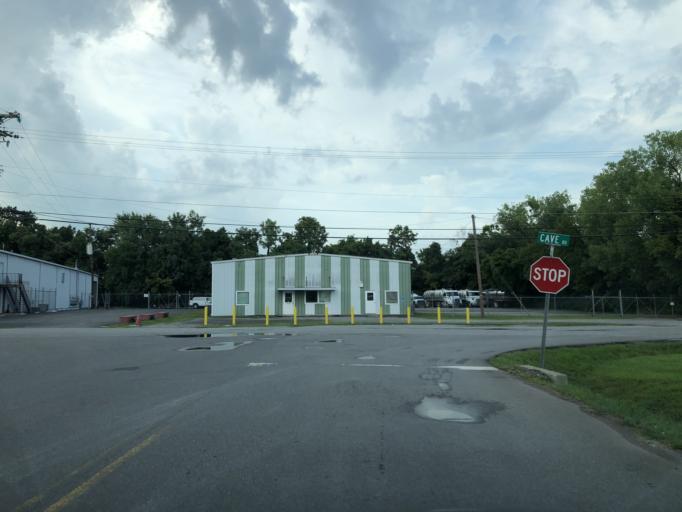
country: US
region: Tennessee
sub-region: Davidson County
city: Nashville
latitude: 36.1617
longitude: -86.7211
